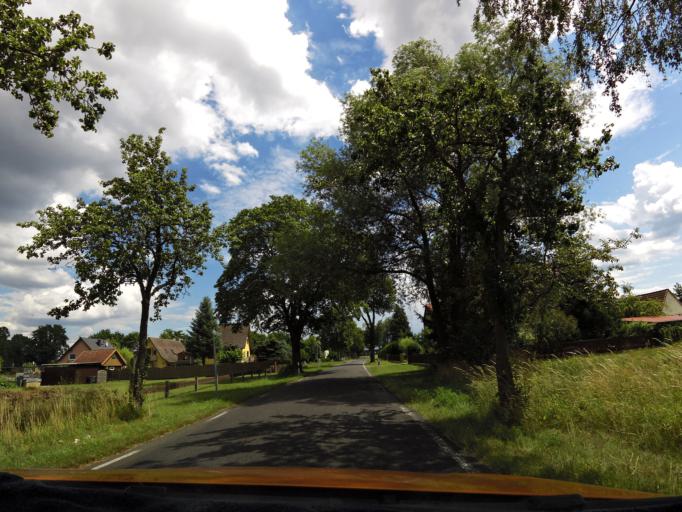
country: DE
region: Brandenburg
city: Storkow
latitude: 52.2472
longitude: 13.8956
